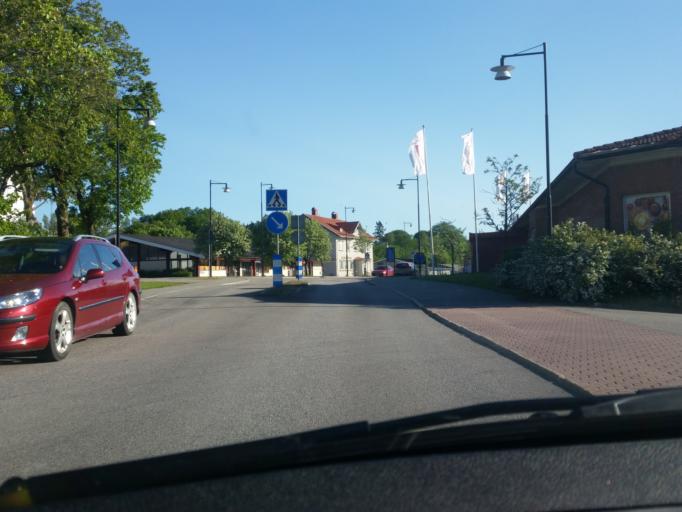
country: SE
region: Vaestra Goetaland
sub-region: Fargelanda Kommun
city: Faergelanda
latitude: 58.5688
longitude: 11.9978
